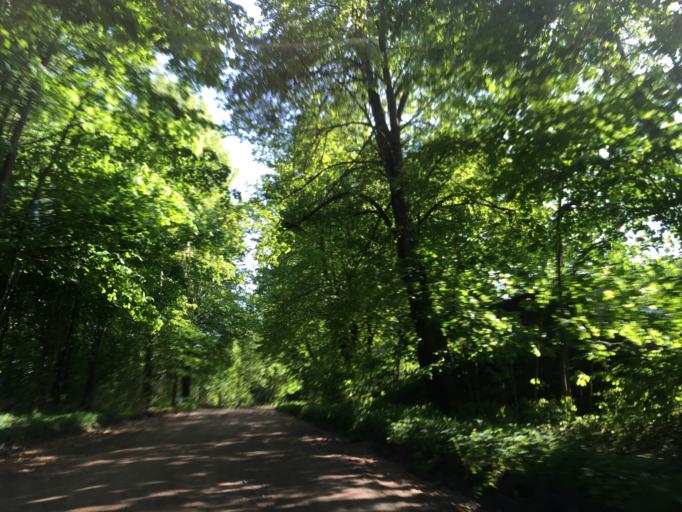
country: LV
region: Ikskile
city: Ikskile
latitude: 56.8261
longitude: 24.4300
